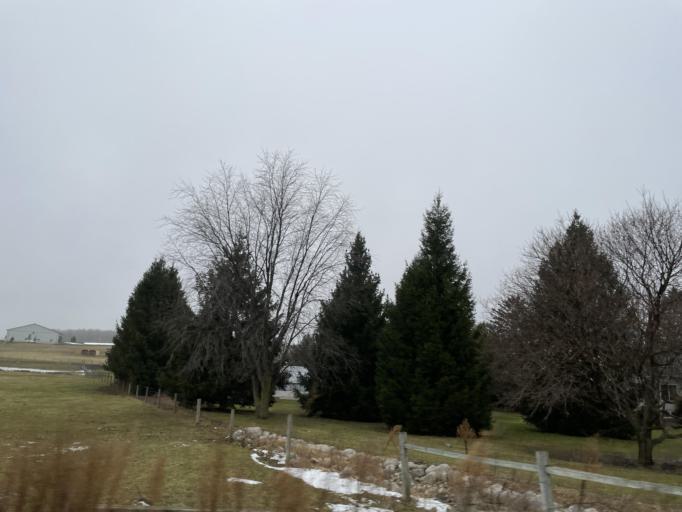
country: CA
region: Ontario
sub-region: Wellington County
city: Guelph
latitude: 43.5004
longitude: -80.3443
